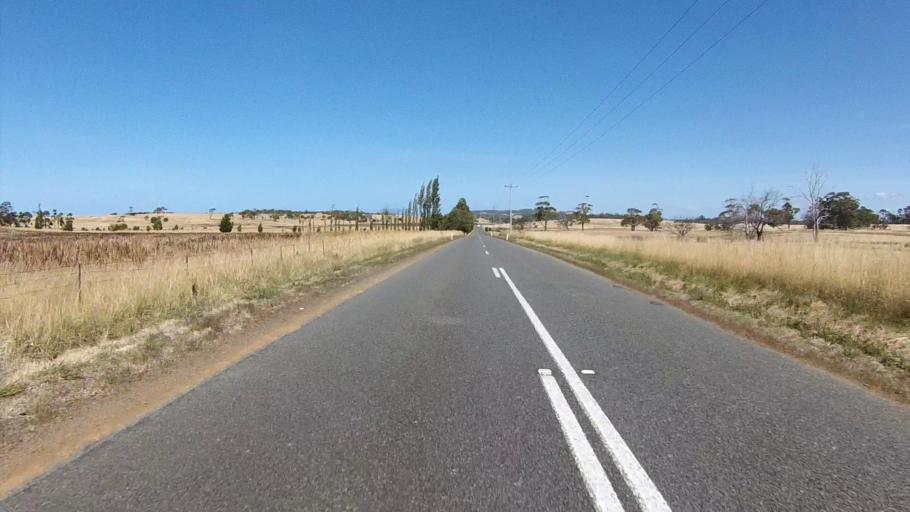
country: AU
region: Tasmania
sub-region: Sorell
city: Sorell
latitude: -42.2694
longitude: 148.0037
